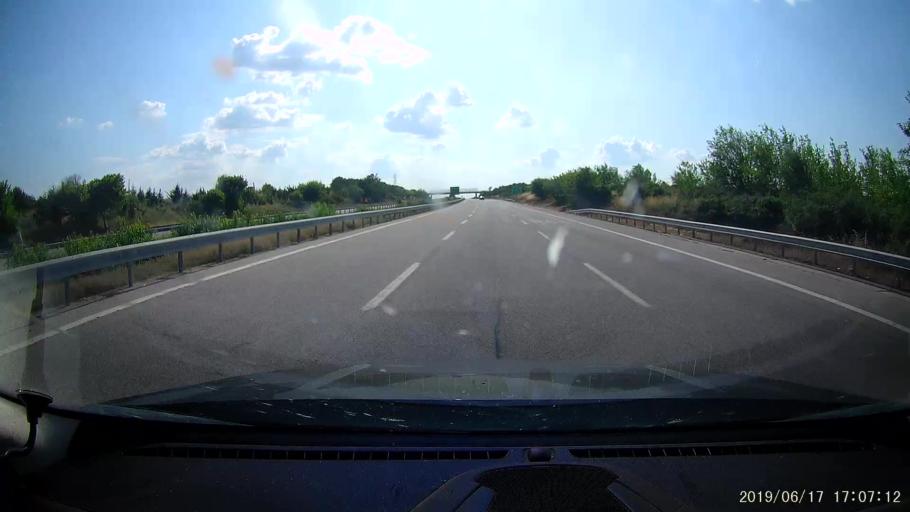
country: TR
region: Edirne
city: Edirne
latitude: 41.6622
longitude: 26.6487
